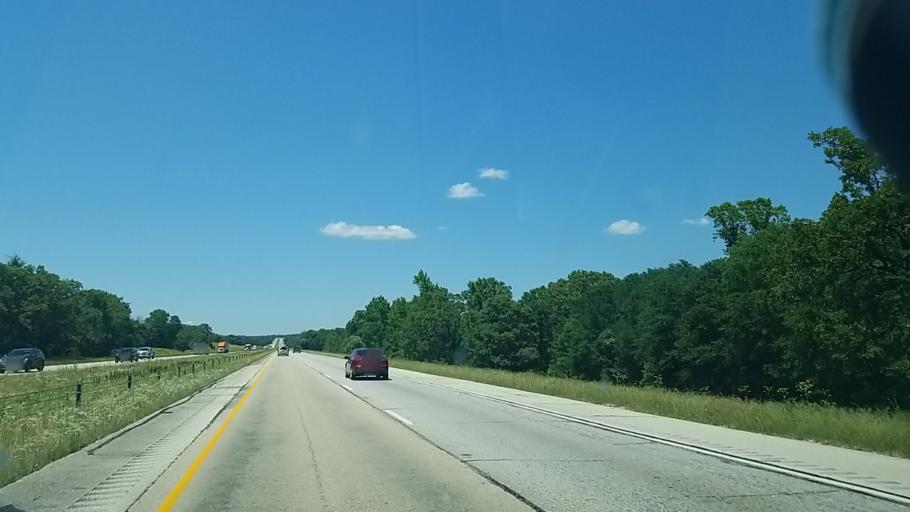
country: US
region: Texas
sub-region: Leon County
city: Centerville
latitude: 31.1715
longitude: -95.9880
